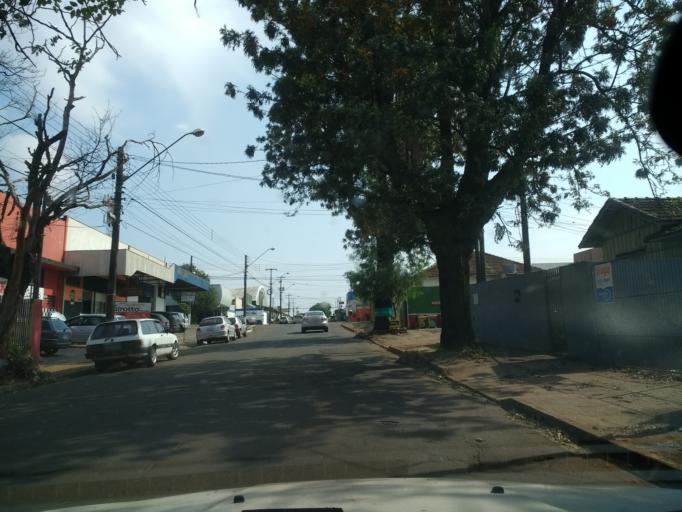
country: BR
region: Parana
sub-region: Londrina
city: Londrina
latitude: -23.2969
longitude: -51.1615
